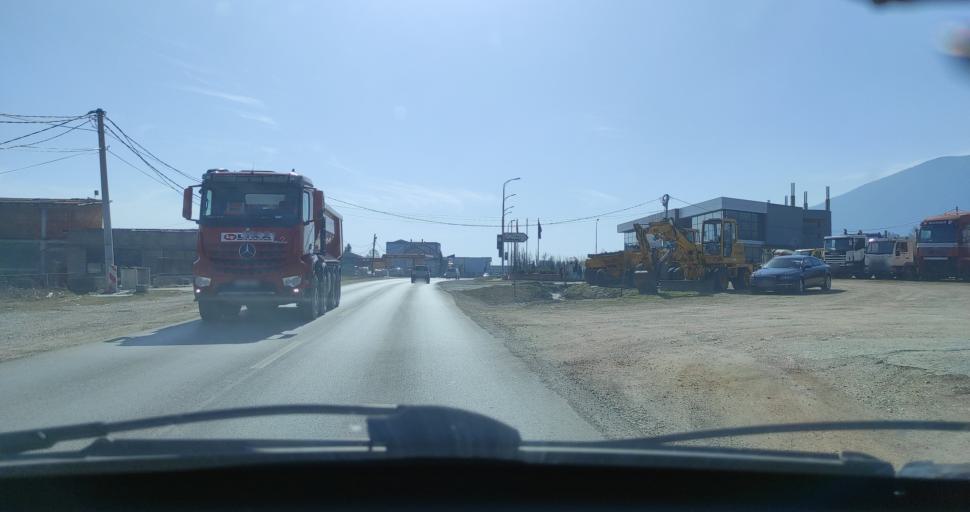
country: XK
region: Pec
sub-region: Komuna e Pejes
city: Peje
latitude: 42.6265
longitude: 20.3052
